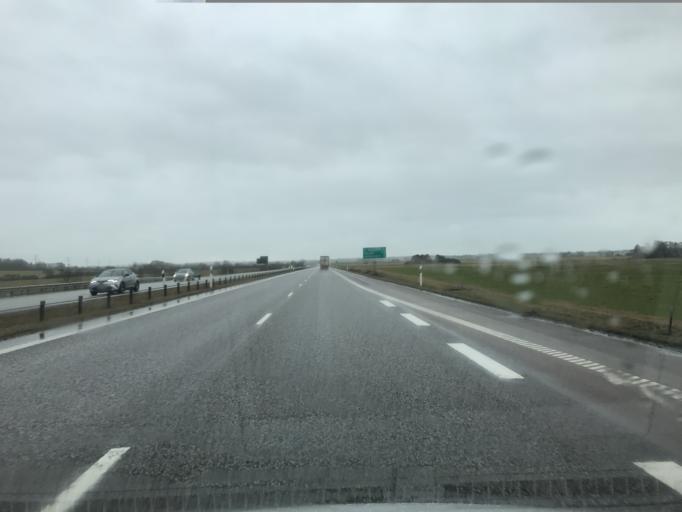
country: SE
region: Skane
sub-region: Angelholms Kommun
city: AEngelholm
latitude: 56.3094
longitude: 12.9097
